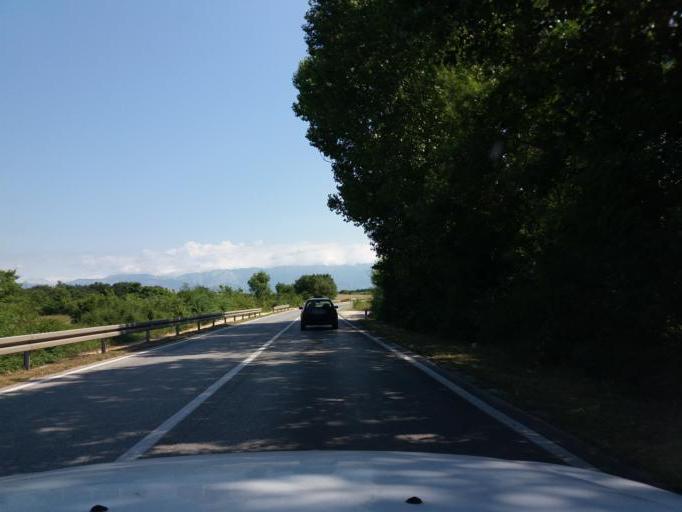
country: HR
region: Zadarska
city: Policnik
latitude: 44.1791
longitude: 15.3870
